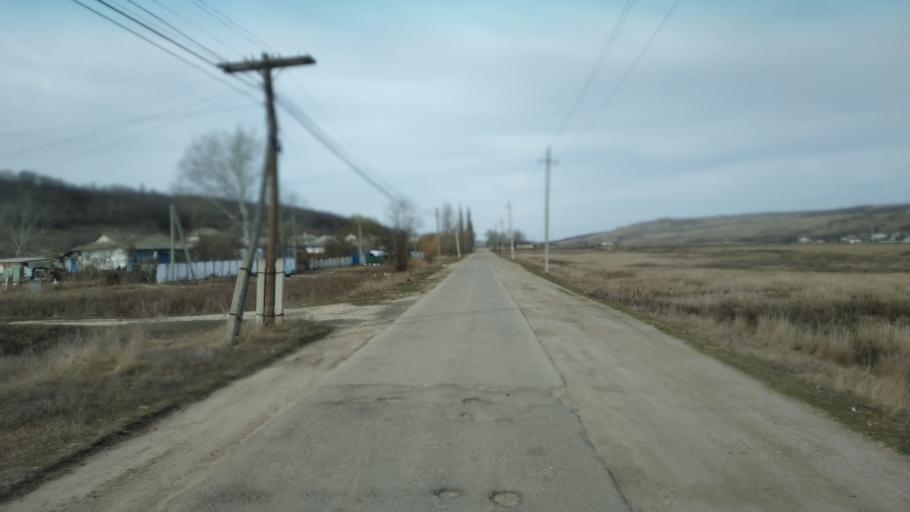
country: RO
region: Vaslui
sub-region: Comuna Dranceni
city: Dranceni
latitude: 46.8677
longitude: 28.1997
